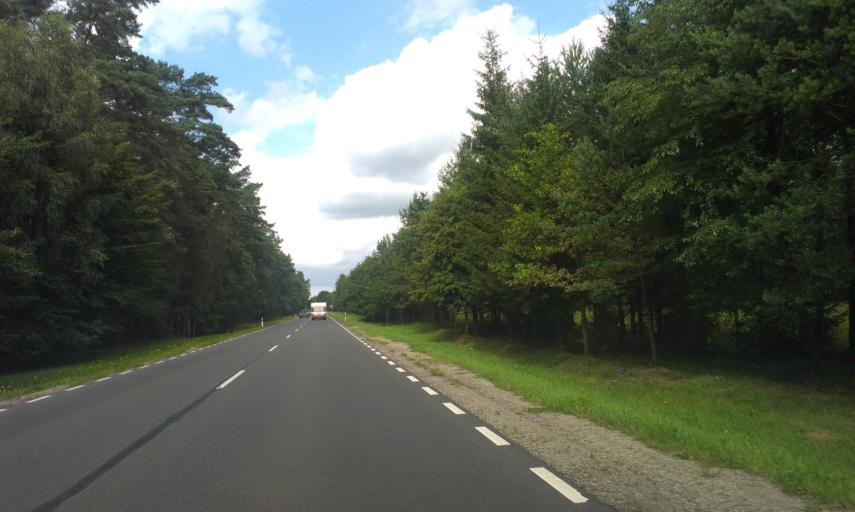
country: PL
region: West Pomeranian Voivodeship
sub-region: Powiat koszalinski
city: Sianow
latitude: 54.0798
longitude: 16.3891
